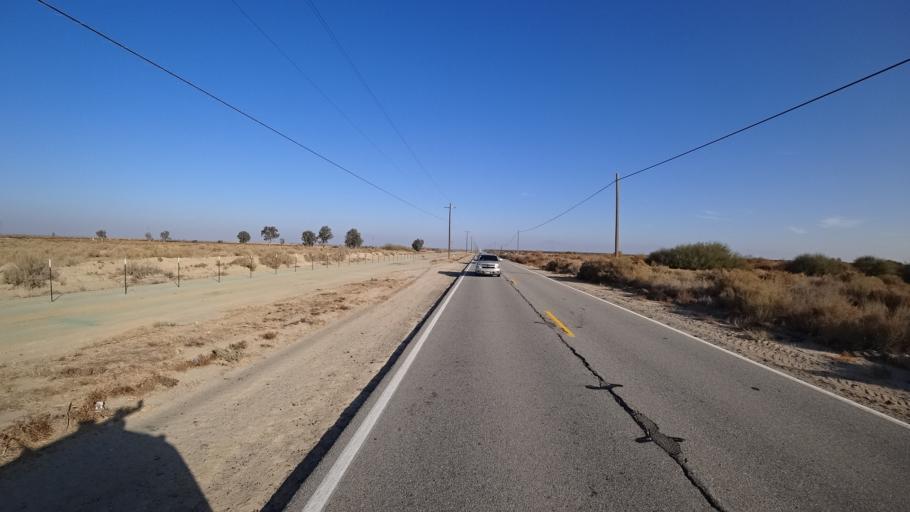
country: US
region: California
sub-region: Kern County
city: Rosedale
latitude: 35.2961
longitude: -119.1929
